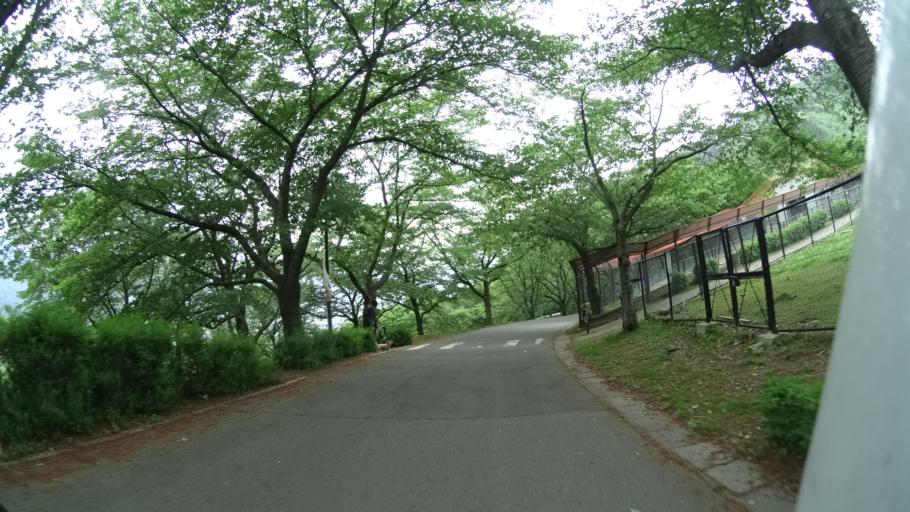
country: JP
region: Nagano
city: Ueda
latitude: 36.4943
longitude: 138.1570
